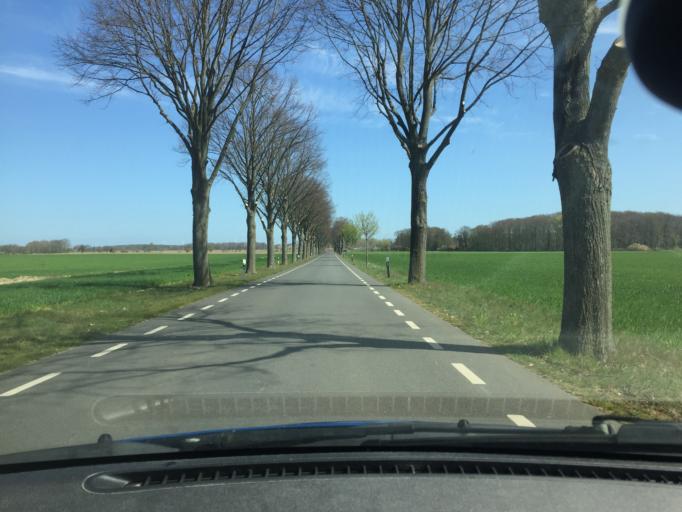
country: DE
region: Lower Saxony
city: Wieren
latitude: 52.9158
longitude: 10.6829
